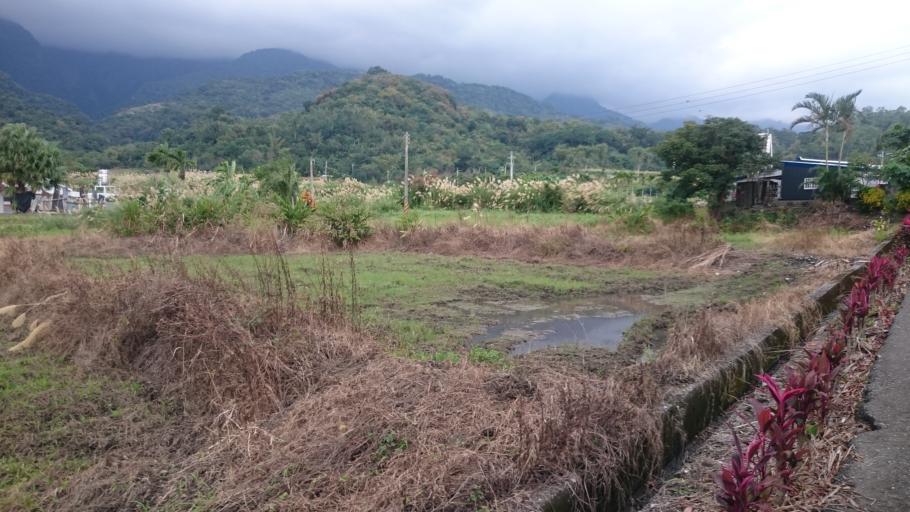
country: TW
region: Taiwan
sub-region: Taitung
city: Taitung
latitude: 23.1943
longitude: 121.3902
